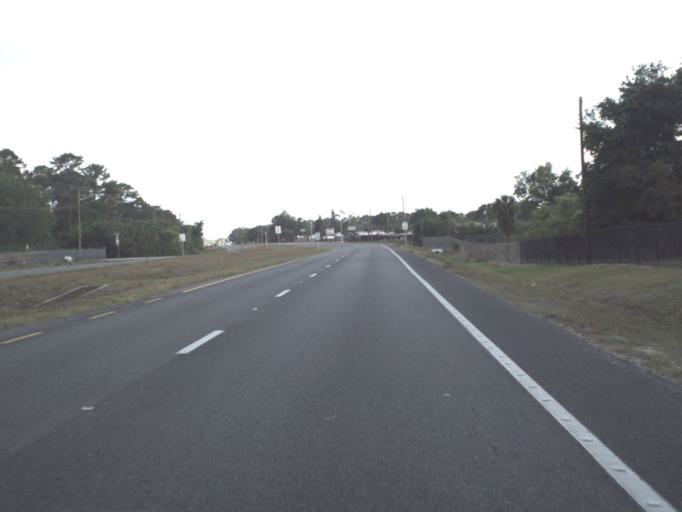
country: US
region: Florida
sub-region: Brevard County
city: Mims
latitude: 28.6939
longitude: -80.8581
